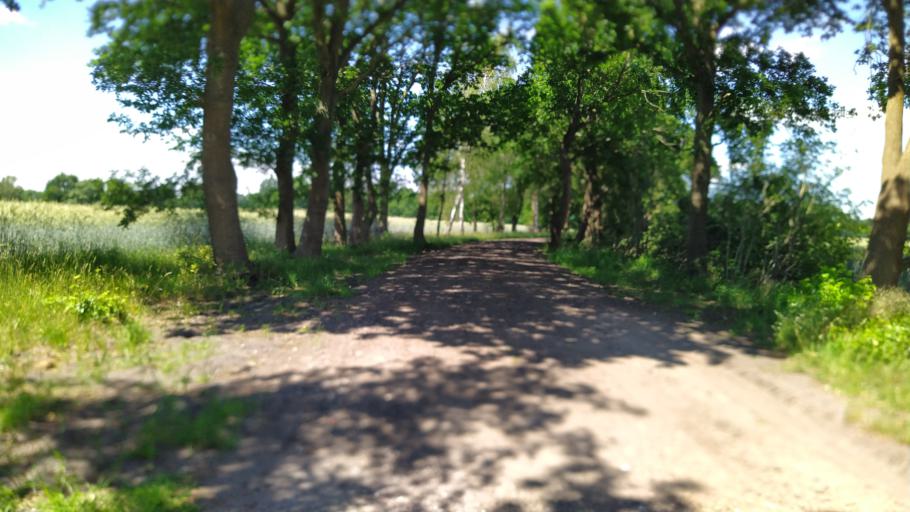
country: DE
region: Lower Saxony
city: Oldendorf
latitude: 53.5651
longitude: 9.2497
